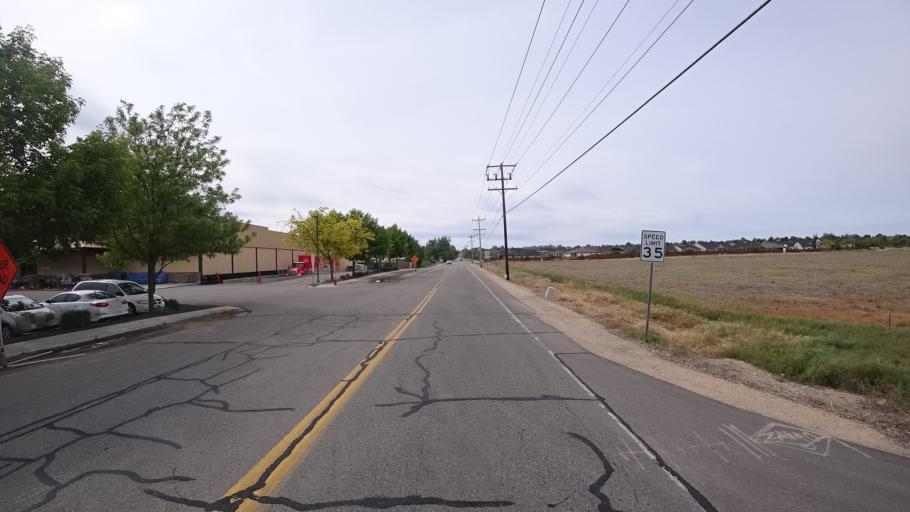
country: US
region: Idaho
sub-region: Ada County
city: Meridian
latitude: 43.5455
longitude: -116.3144
